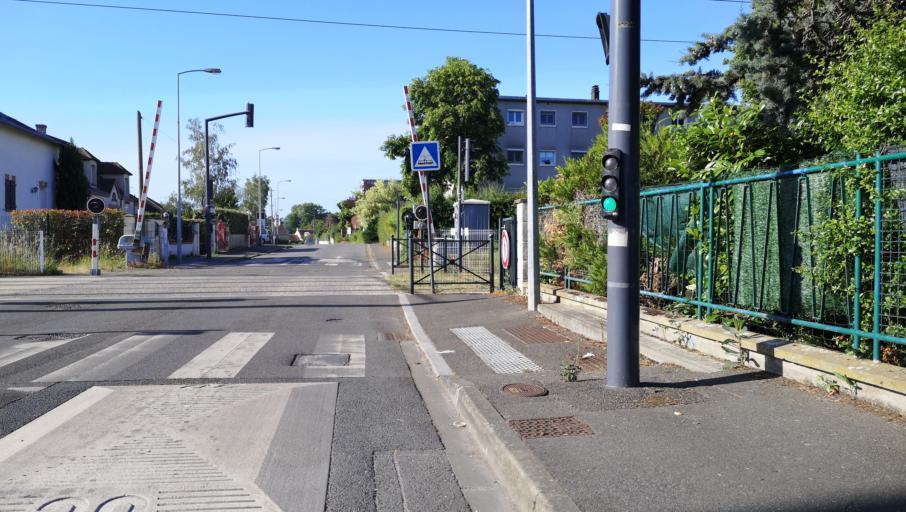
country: FR
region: Centre
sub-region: Departement du Loiret
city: Saint-Jean-de-Braye
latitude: 47.9096
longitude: 1.9637
